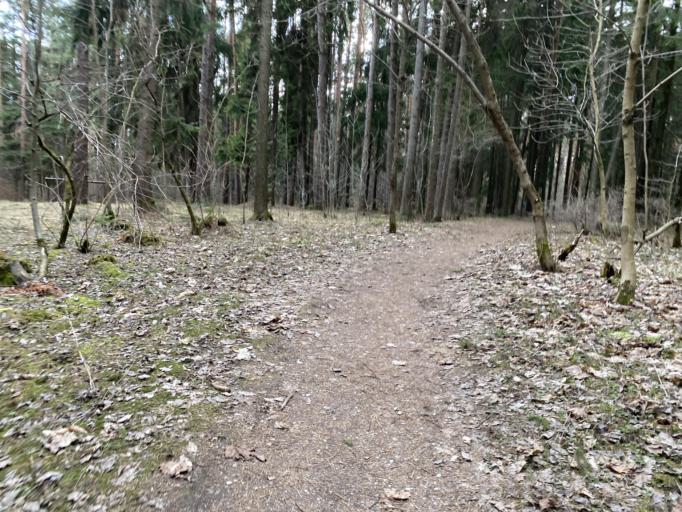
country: BY
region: Minsk
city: Borovlyany
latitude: 53.9471
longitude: 27.6540
